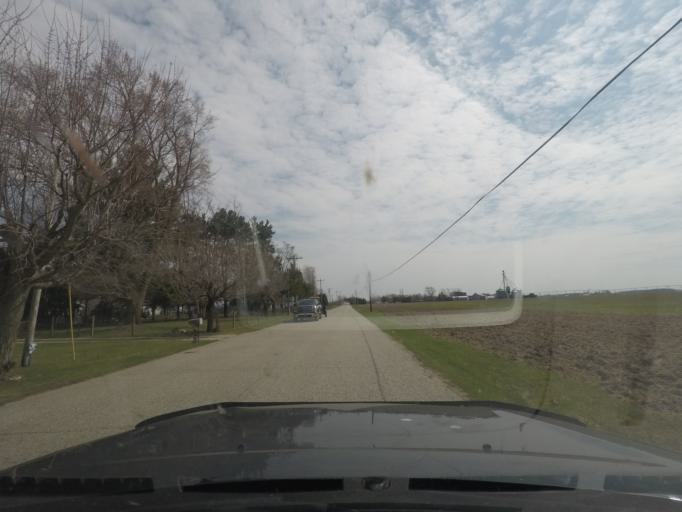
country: US
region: Indiana
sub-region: LaPorte County
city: Kingsford Heights
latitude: 41.4749
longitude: -86.6756
